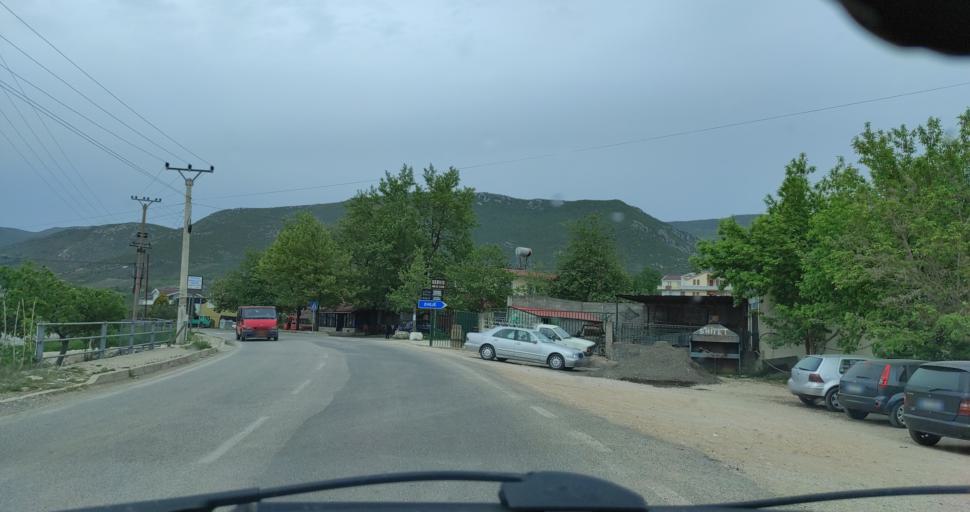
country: AL
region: Lezhe
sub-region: Rrethi i Kurbinit
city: Lac
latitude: 41.6065
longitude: 19.7117
